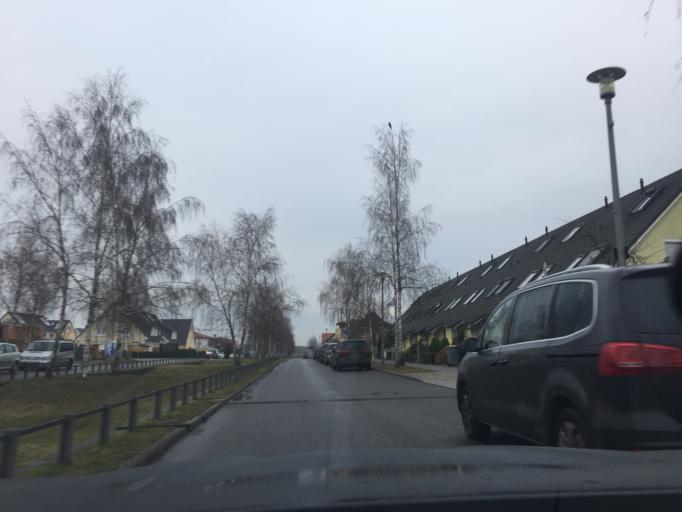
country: DE
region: Berlin
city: Kladow
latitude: 52.4699
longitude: 13.1305
